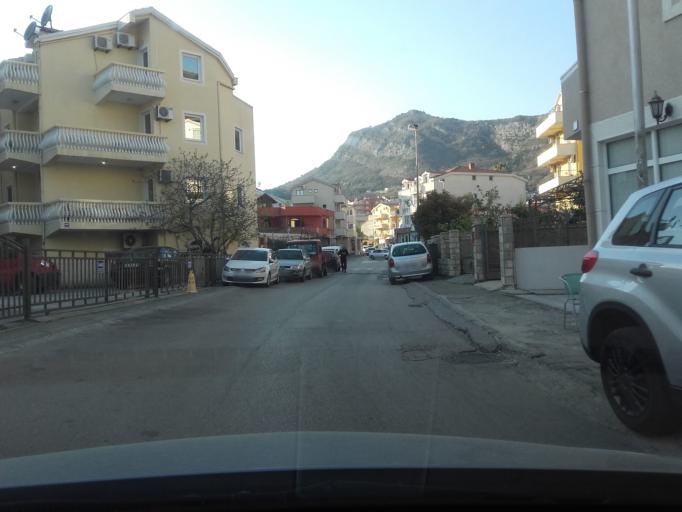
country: ME
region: Budva
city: Budva
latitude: 42.2907
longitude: 18.8475
